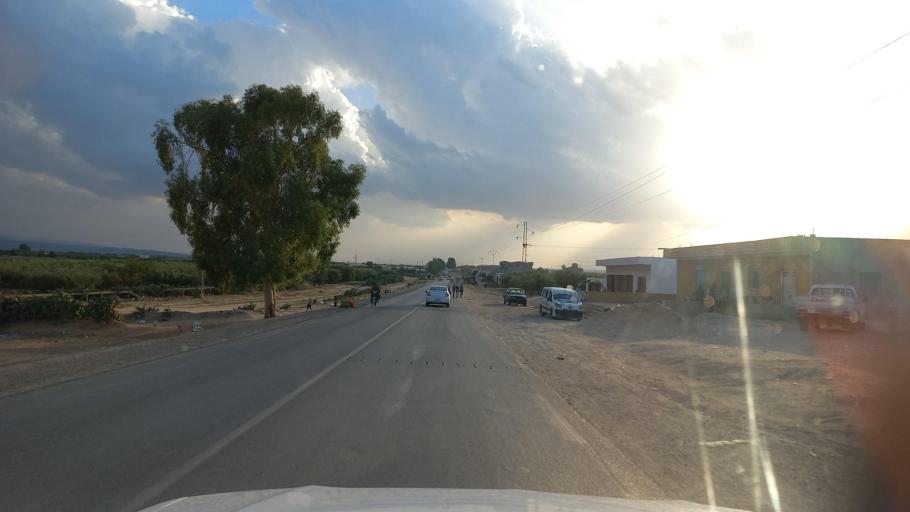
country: TN
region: Al Qasrayn
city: Kasserine
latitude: 35.2683
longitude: 9.0683
